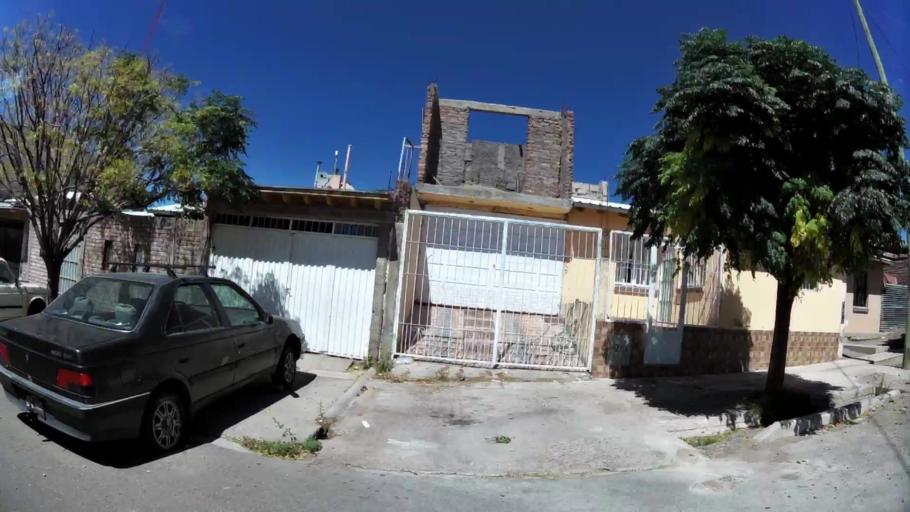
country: AR
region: Mendoza
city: Las Heras
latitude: -32.8523
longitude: -68.8737
